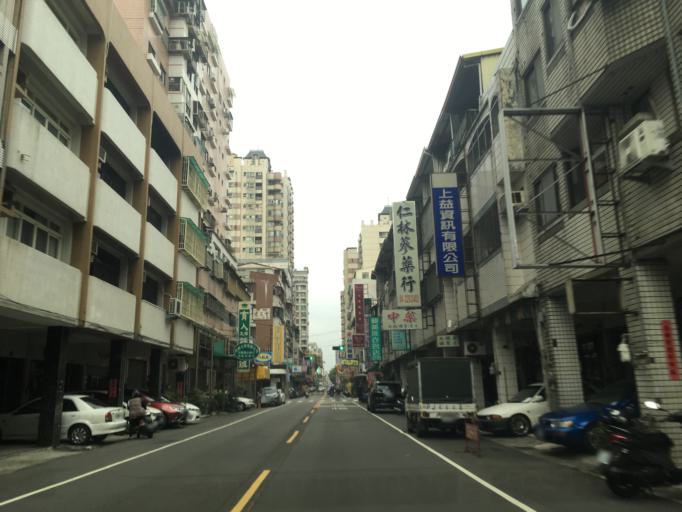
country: TW
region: Taiwan
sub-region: Taichung City
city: Taichung
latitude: 24.1743
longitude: 120.6776
